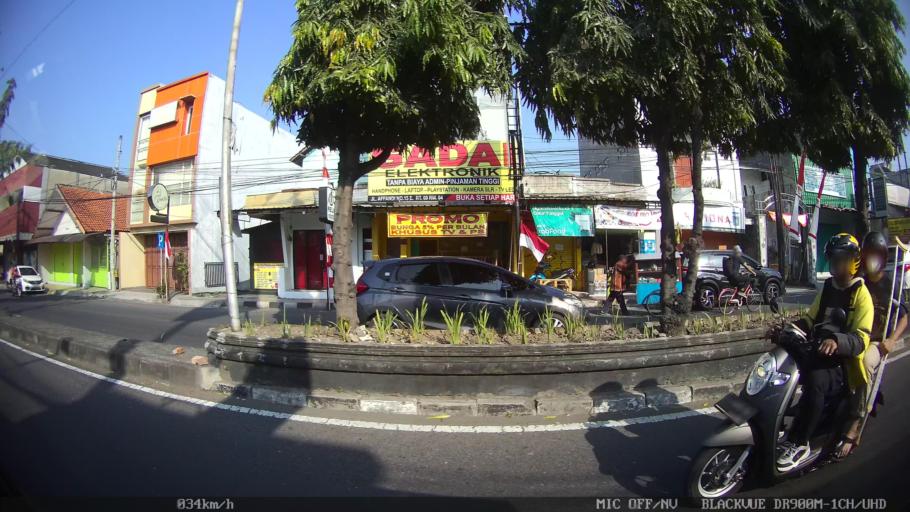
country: ID
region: Daerah Istimewa Yogyakarta
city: Yogyakarta
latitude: -7.7724
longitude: 110.3893
